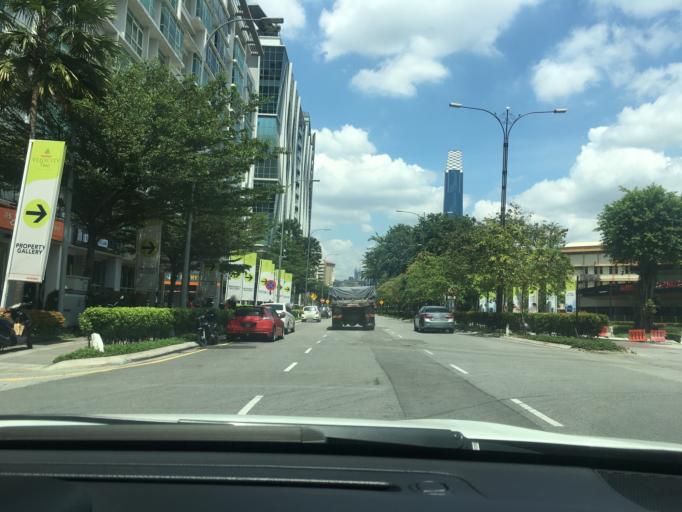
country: MY
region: Kuala Lumpur
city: Kuala Lumpur
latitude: 3.1285
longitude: 101.7245
